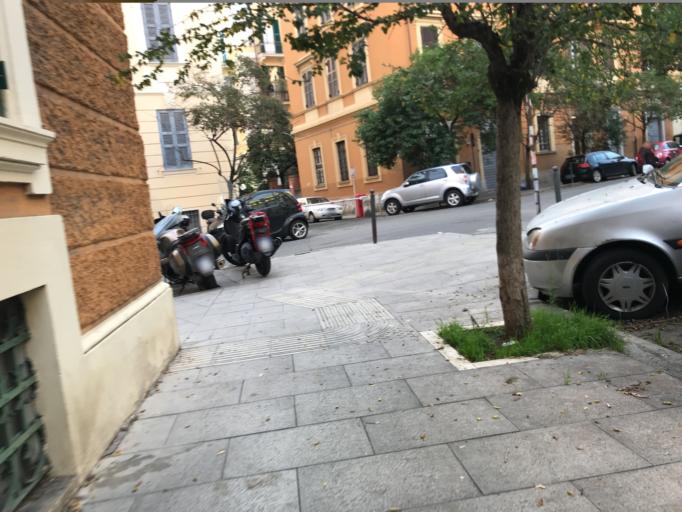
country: IT
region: Latium
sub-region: Citta metropolitana di Roma Capitale
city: Rome
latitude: 41.9095
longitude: 12.5174
